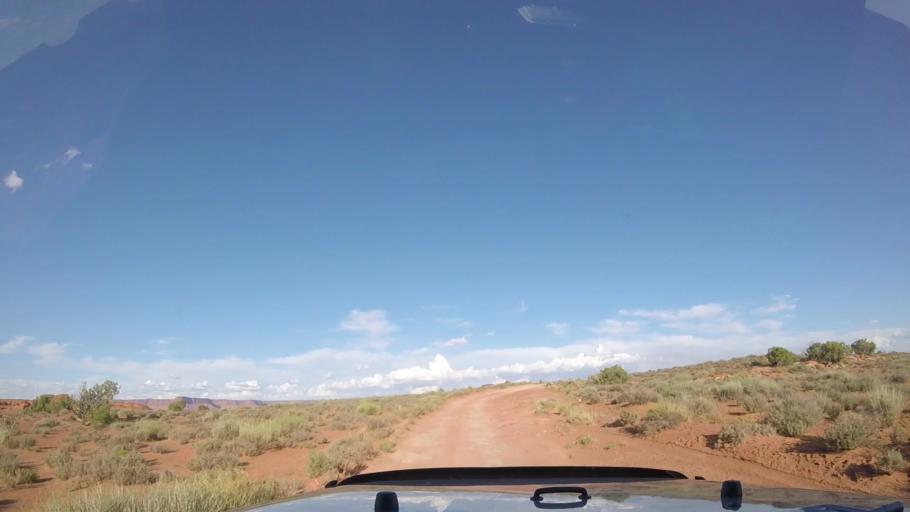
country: US
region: Utah
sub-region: Grand County
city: Moab
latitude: 38.2155
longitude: -109.7943
